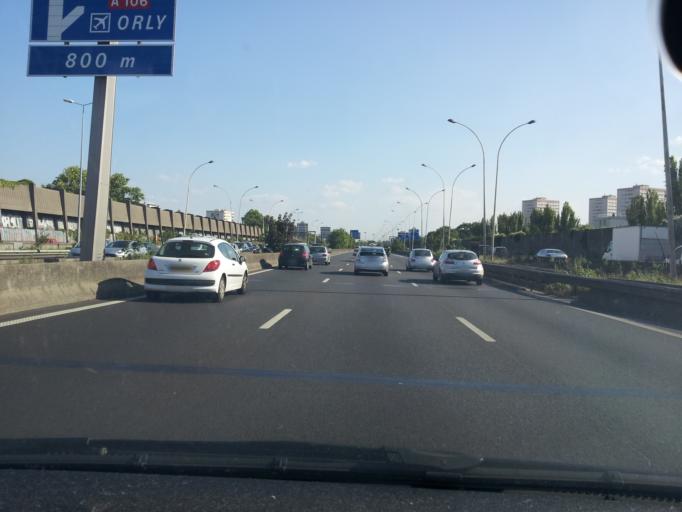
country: FR
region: Ile-de-France
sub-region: Departement du Val-de-Marne
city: L'Hay-les-Roses
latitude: 48.7785
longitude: 2.3462
